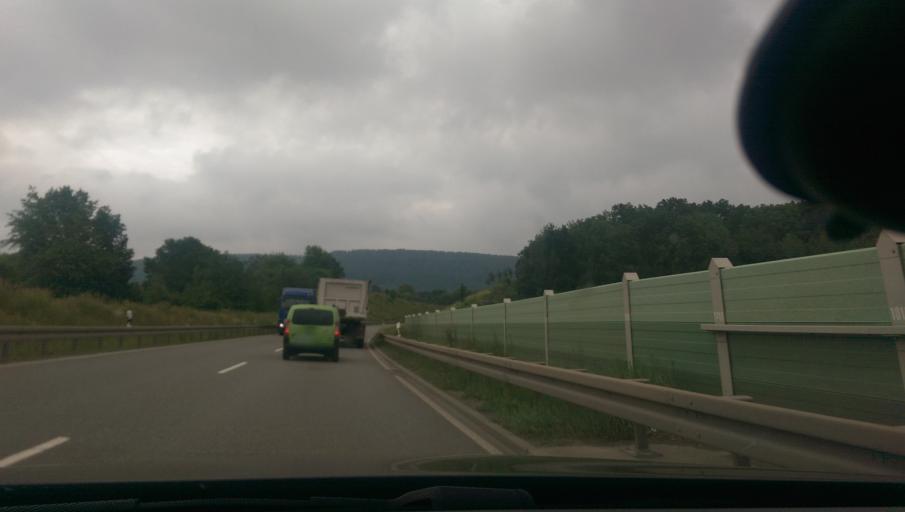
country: DE
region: Thuringia
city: Sondershausen
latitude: 51.3764
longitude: 10.8493
